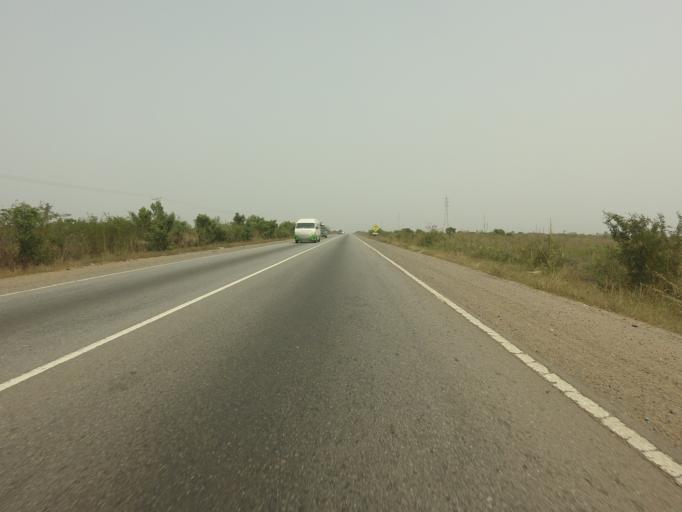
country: GH
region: Greater Accra
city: Tema
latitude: 5.7898
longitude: 0.1140
